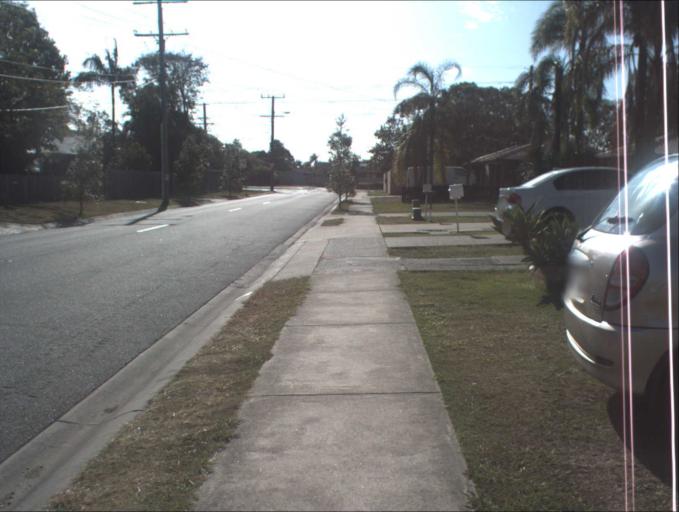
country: AU
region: Queensland
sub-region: Logan
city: Beenleigh
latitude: -27.6829
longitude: 153.1822
